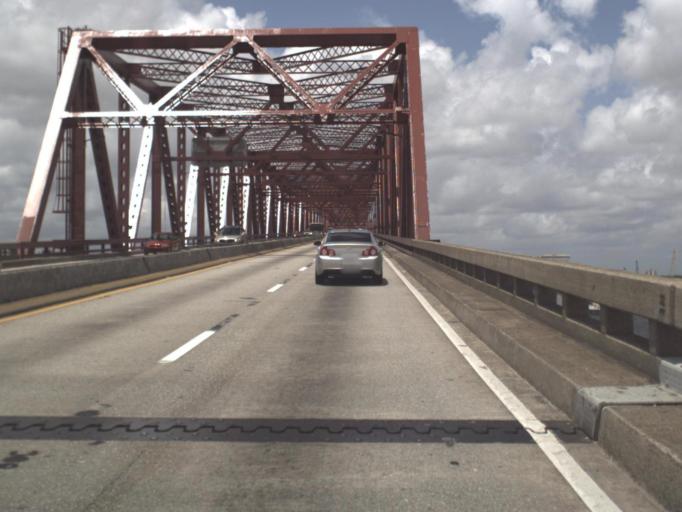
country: US
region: Florida
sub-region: Duval County
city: Jacksonville
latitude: 30.3273
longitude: -81.6182
